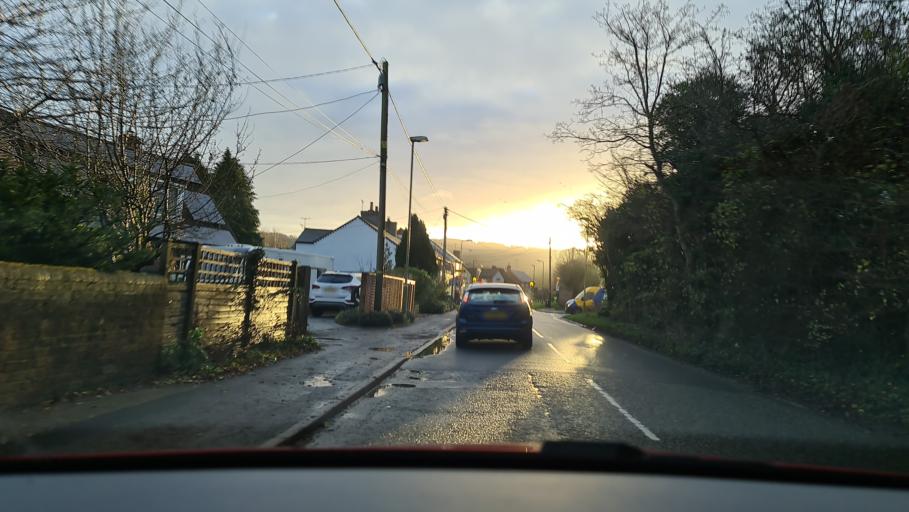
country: GB
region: England
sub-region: Oxfordshire
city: Chinnor
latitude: 51.7054
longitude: -0.9146
